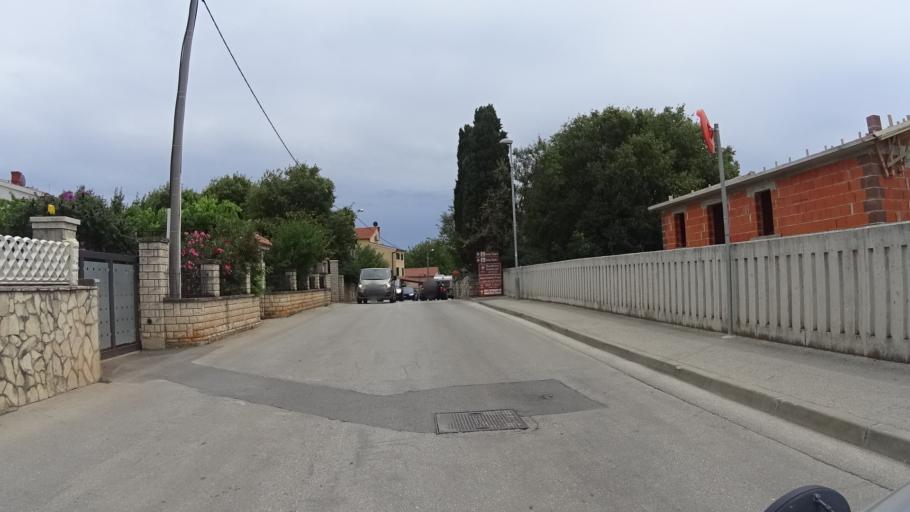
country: HR
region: Istarska
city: Medulin
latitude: 44.8040
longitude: 13.9099
